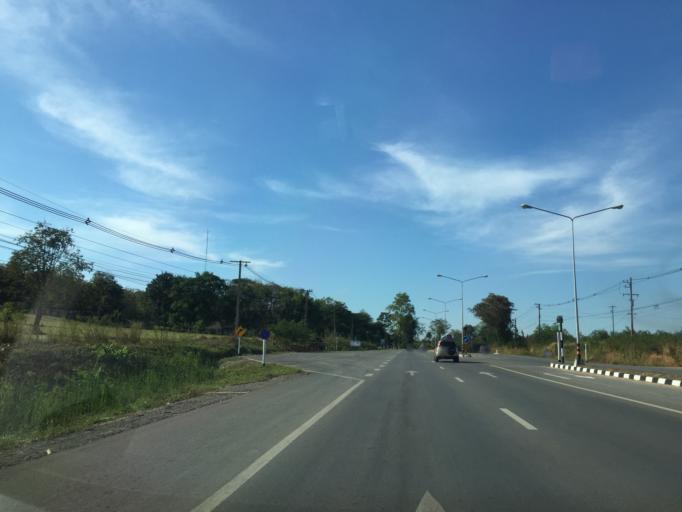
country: TH
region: Loei
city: Wang Saphung
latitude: 17.2977
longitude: 101.8125
